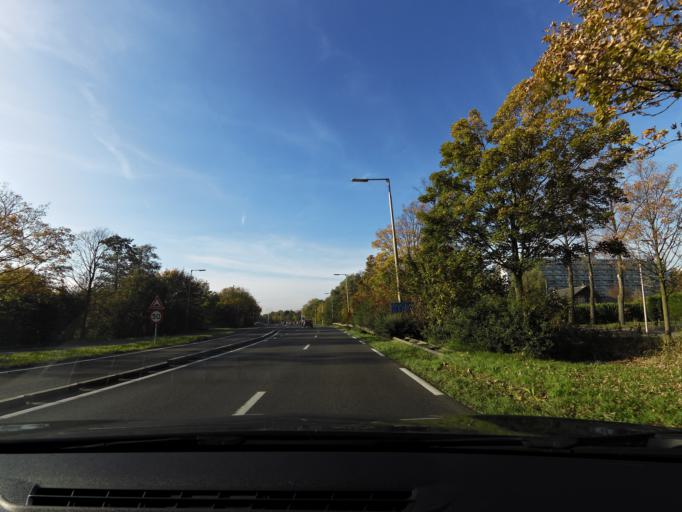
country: NL
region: South Holland
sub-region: Gemeente Ridderkerk
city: Ridderkerk
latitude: 51.8854
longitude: 4.5842
